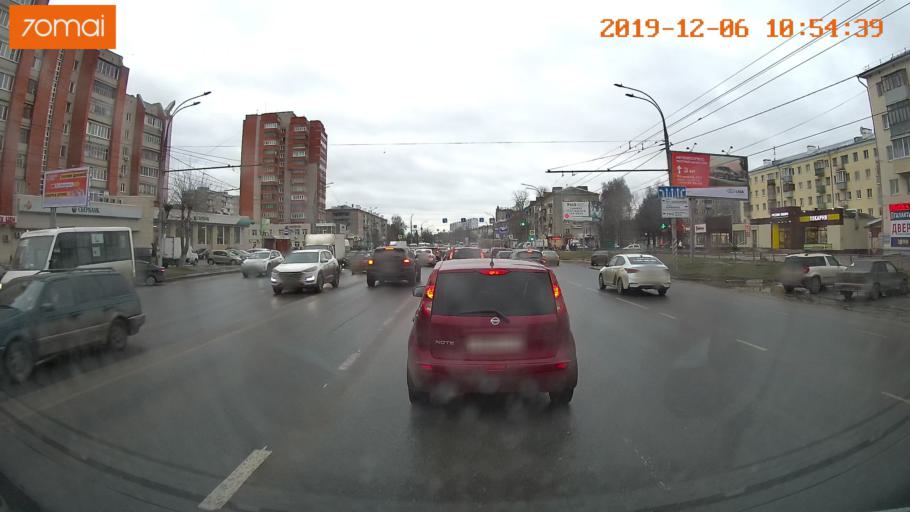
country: RU
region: Ivanovo
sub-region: Gorod Ivanovo
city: Ivanovo
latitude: 56.9727
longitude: 40.9740
